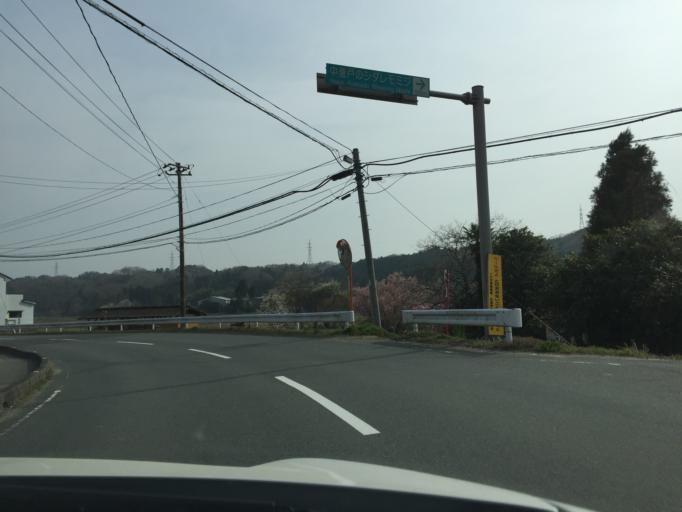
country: JP
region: Fukushima
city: Iwaki
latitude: 36.9650
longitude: 140.8106
